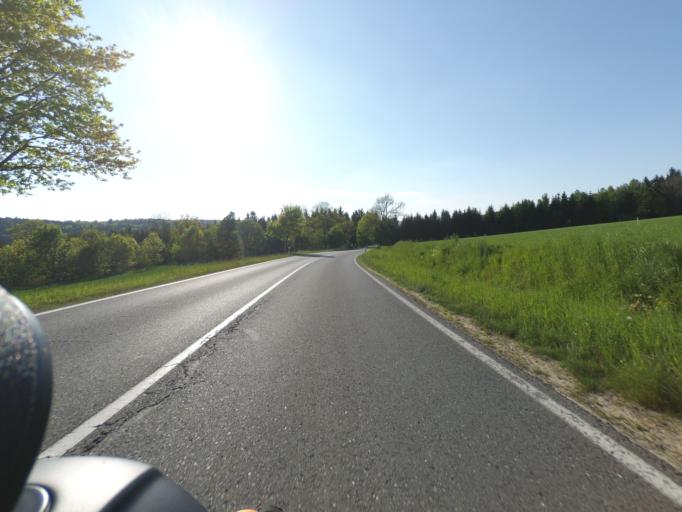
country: DE
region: Saxony
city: Obercunnersdorf
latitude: 50.8800
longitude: 13.5715
